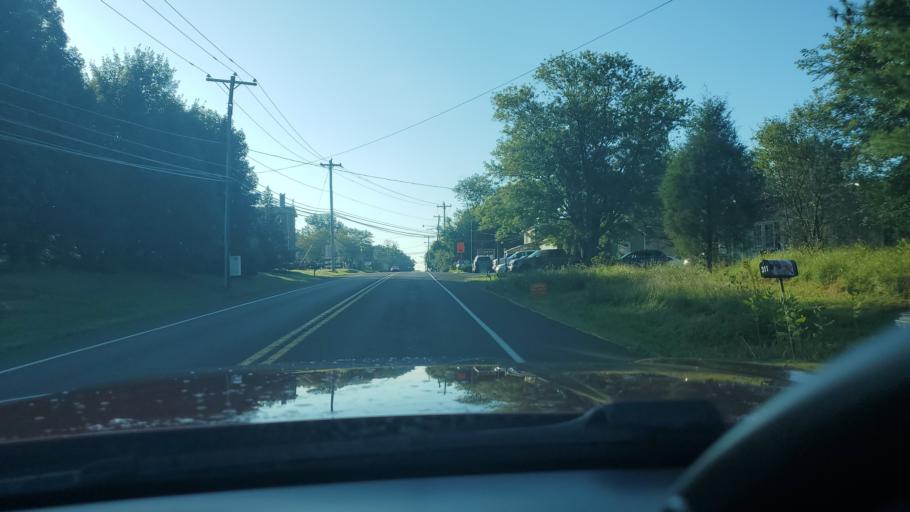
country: US
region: Pennsylvania
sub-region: Montgomery County
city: Harleysville
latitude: 40.2985
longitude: -75.4111
